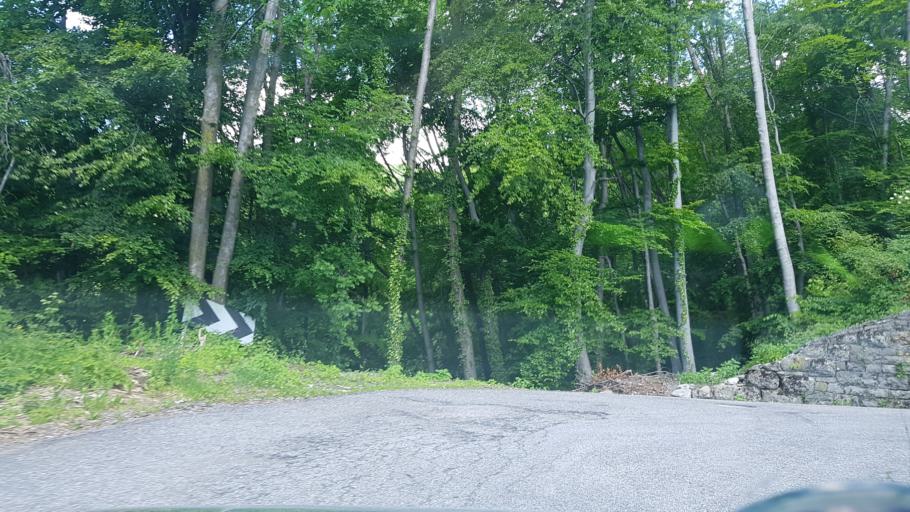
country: IT
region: Friuli Venezia Giulia
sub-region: Provincia di Udine
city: Torreano
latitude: 46.1741
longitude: 13.4299
